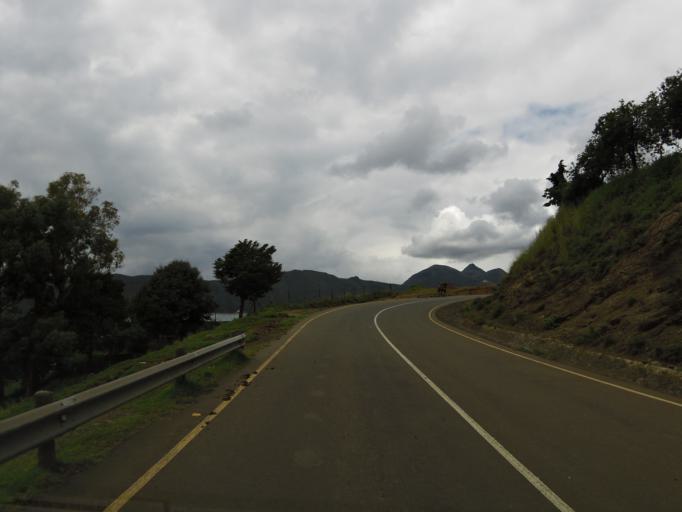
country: LS
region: Butha-Buthe
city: Butha-Buthe
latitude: -29.0358
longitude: 28.2901
